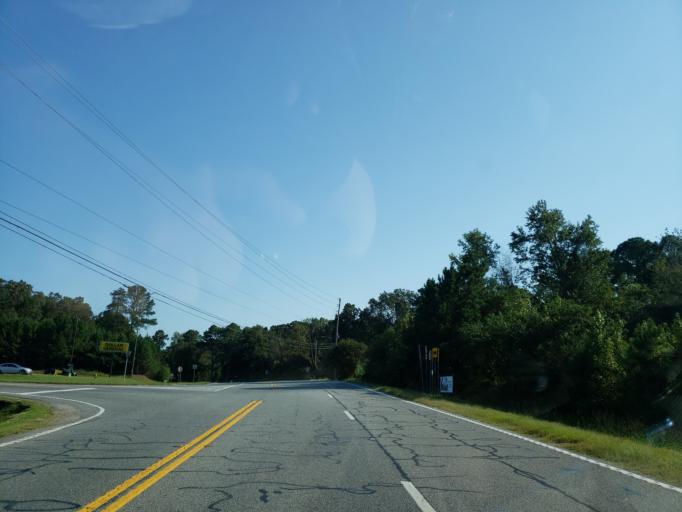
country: US
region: Georgia
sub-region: Whitfield County
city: Varnell
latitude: 34.8985
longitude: -84.9767
